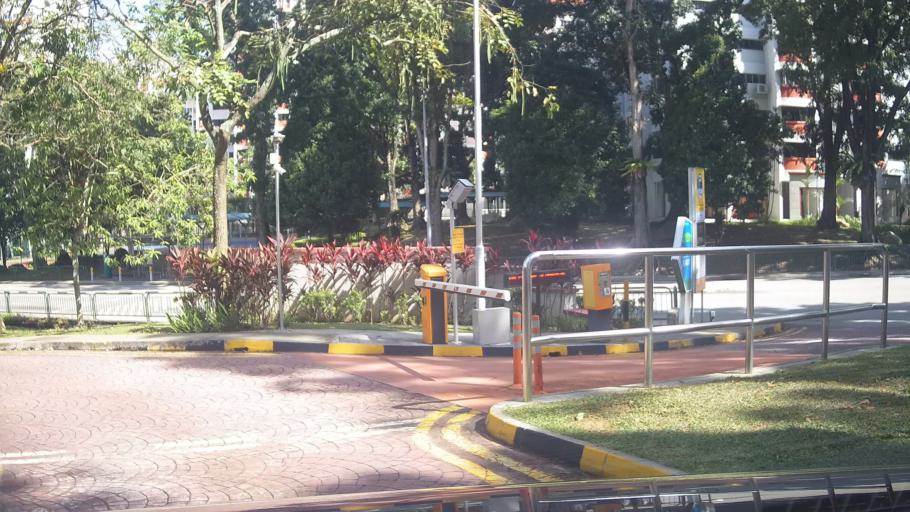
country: MY
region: Johor
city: Johor Bahru
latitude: 1.4403
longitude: 103.7769
